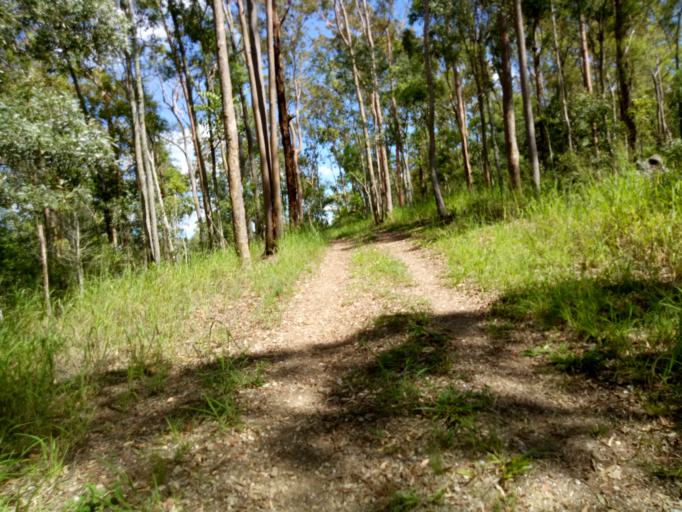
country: AU
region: Queensland
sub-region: Moreton Bay
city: Ferny Hills
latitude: -27.4455
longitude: 152.9101
